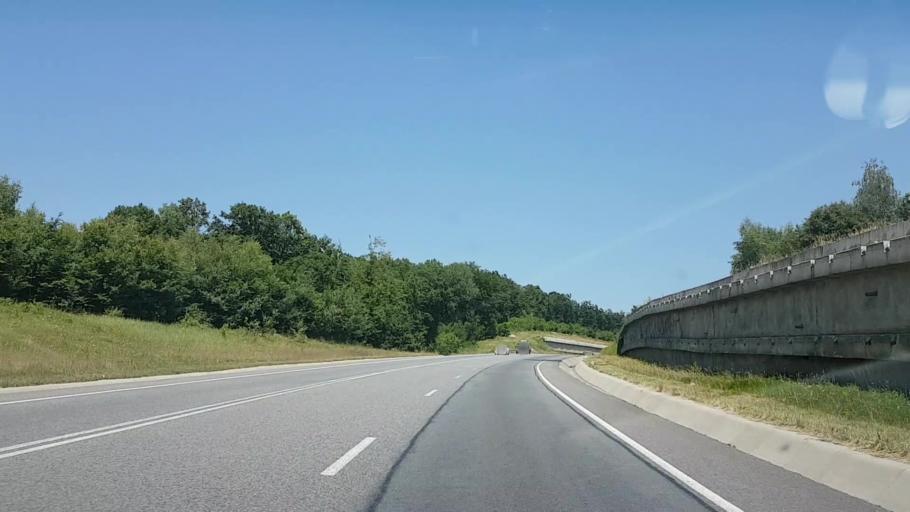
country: RO
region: Cluj
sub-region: Comuna Feleacu
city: Feleacu
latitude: 46.7088
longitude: 23.6451
